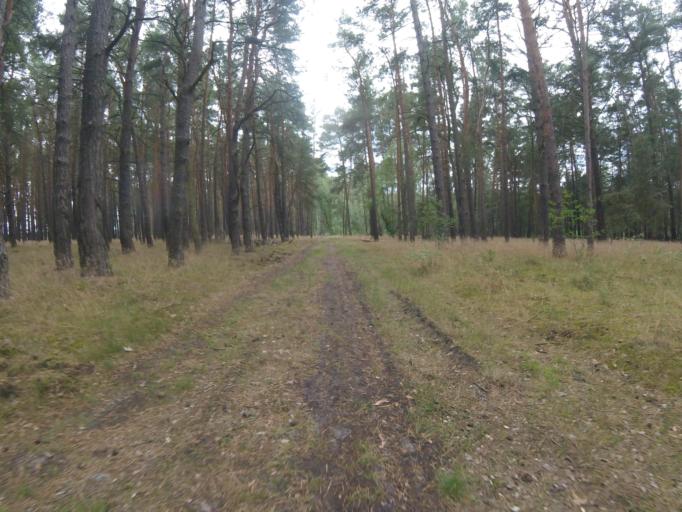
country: DE
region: Brandenburg
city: Bestensee
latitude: 52.2712
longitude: 13.7143
